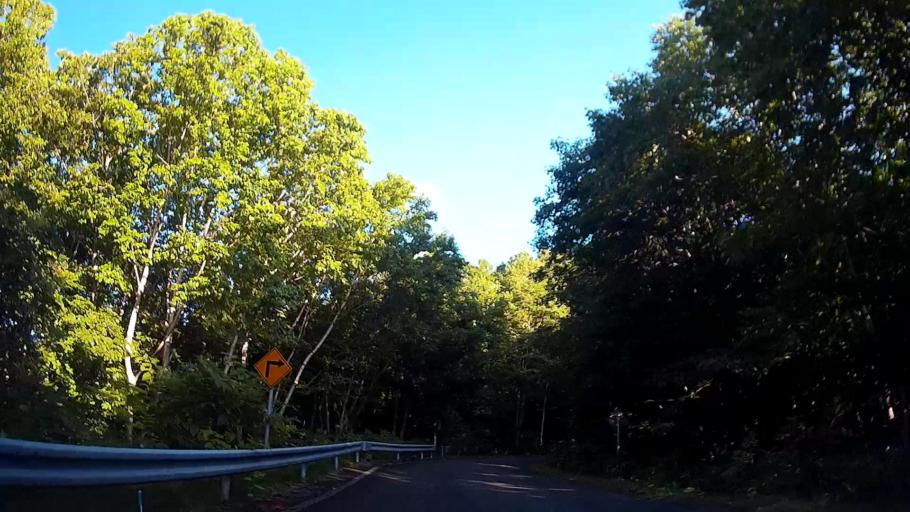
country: JP
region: Hokkaido
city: Iwanai
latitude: 42.6455
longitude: 140.0332
